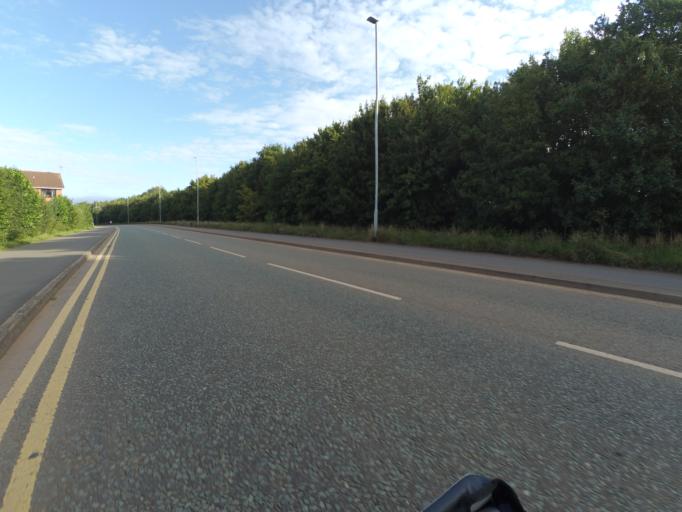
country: GB
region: England
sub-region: Staffordshire
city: Stafford
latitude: 52.8045
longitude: -2.1294
